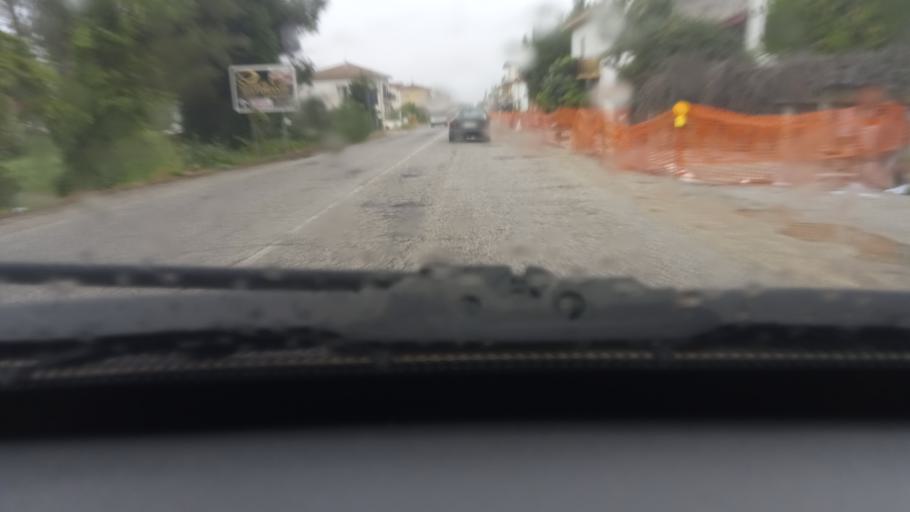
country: IT
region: Latium
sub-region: Provincia di Latina
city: Minturno
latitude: 41.2522
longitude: 13.7265
